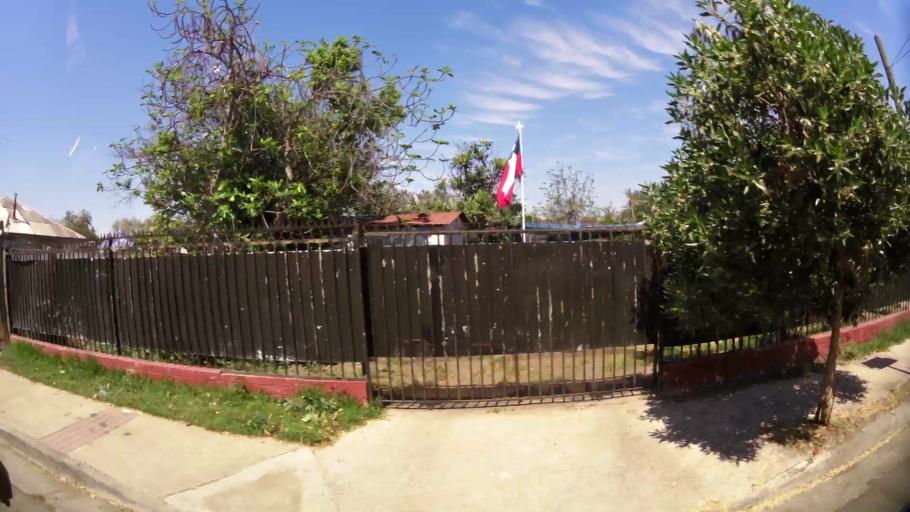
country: CL
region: Santiago Metropolitan
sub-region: Provincia de Talagante
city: Talagante
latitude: -33.6563
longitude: -70.9301
